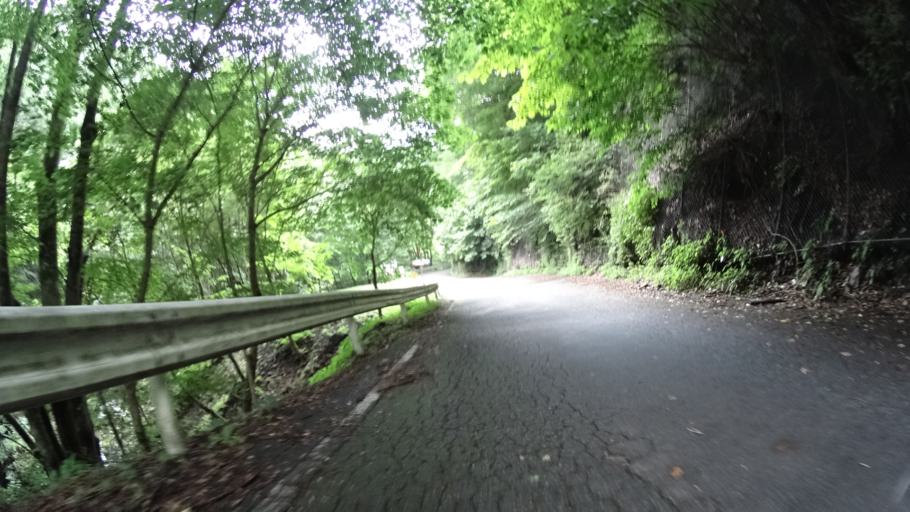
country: JP
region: Nagano
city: Saku
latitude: 36.0651
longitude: 138.6826
